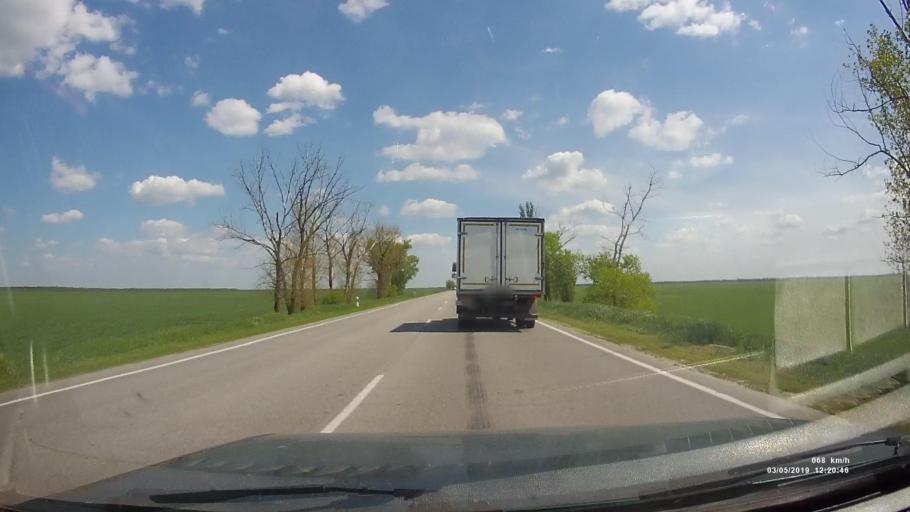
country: RU
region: Rostov
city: Melikhovskaya
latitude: 47.4049
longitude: 40.6270
